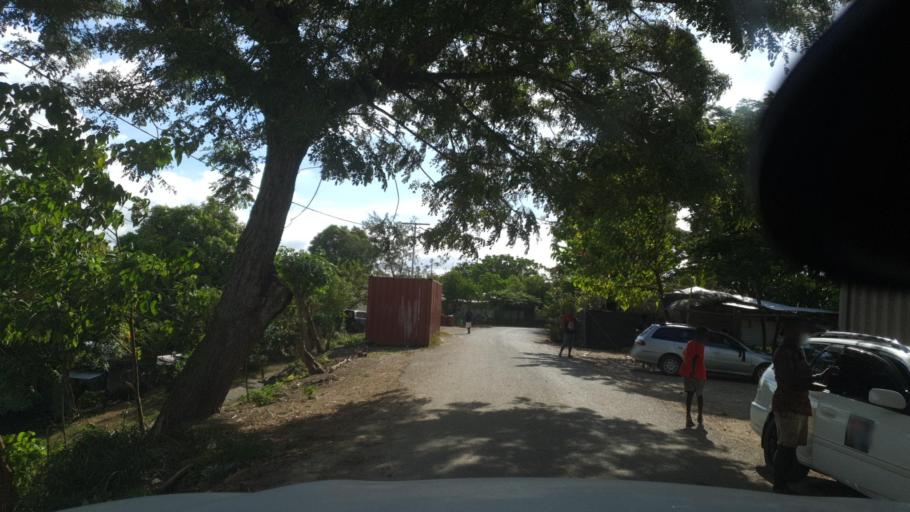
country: SB
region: Guadalcanal
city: Honiara
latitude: -9.4385
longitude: 159.9469
